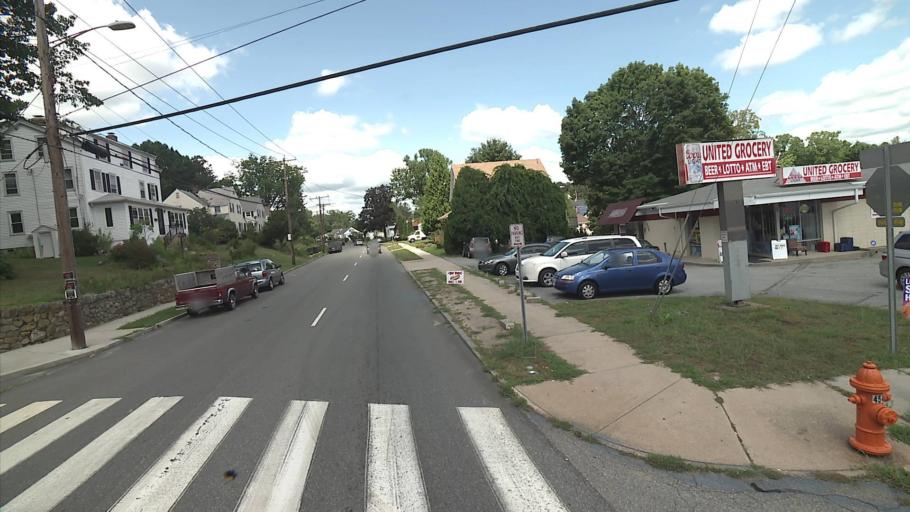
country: US
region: Connecticut
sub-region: New London County
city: New London
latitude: 41.3559
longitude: -72.1119
